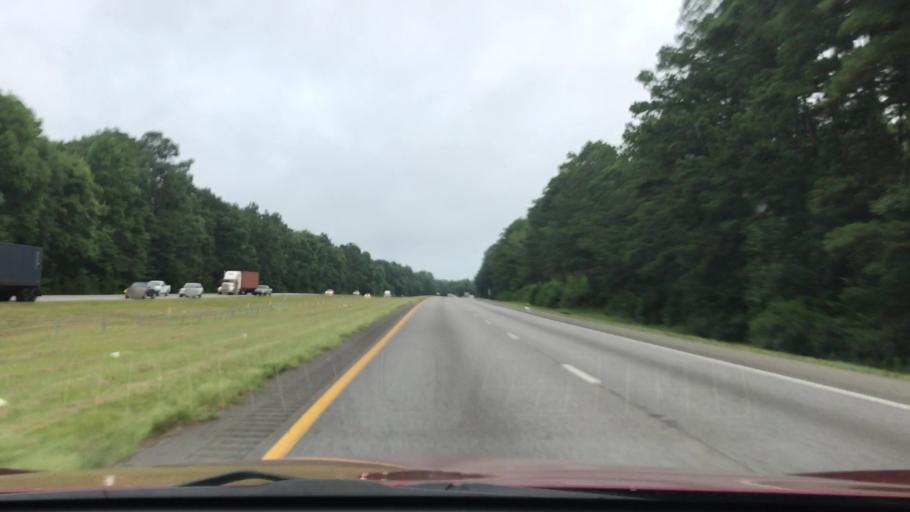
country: US
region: South Carolina
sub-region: Dorchester County
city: Ridgeville
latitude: 33.0921
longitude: -80.2277
